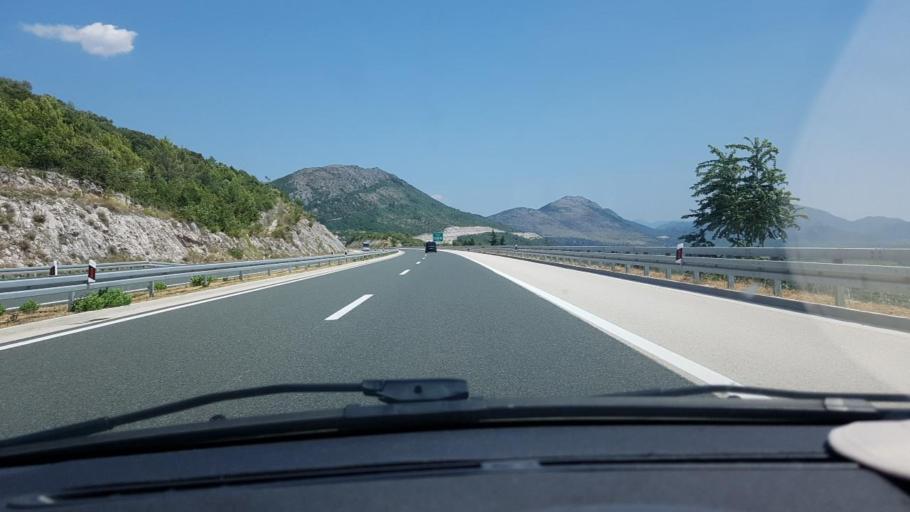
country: HR
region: Splitsko-Dalmatinska
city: Vrgorac
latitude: 43.1817
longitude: 17.4055
